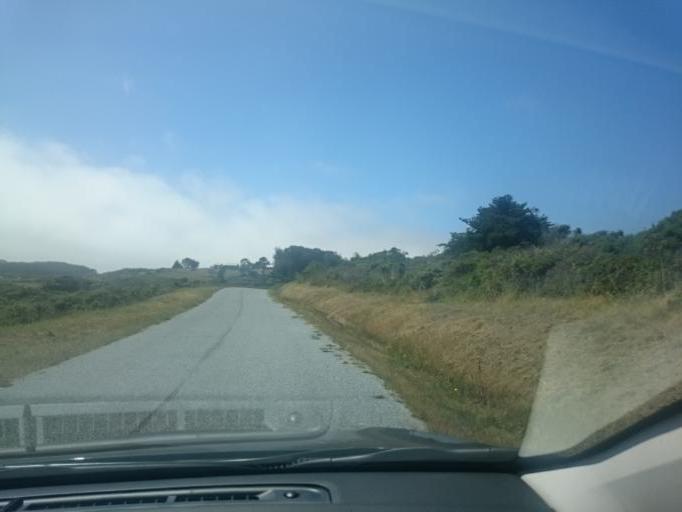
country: US
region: California
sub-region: San Mateo County
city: Portola Valley
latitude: 37.1845
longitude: -122.3806
